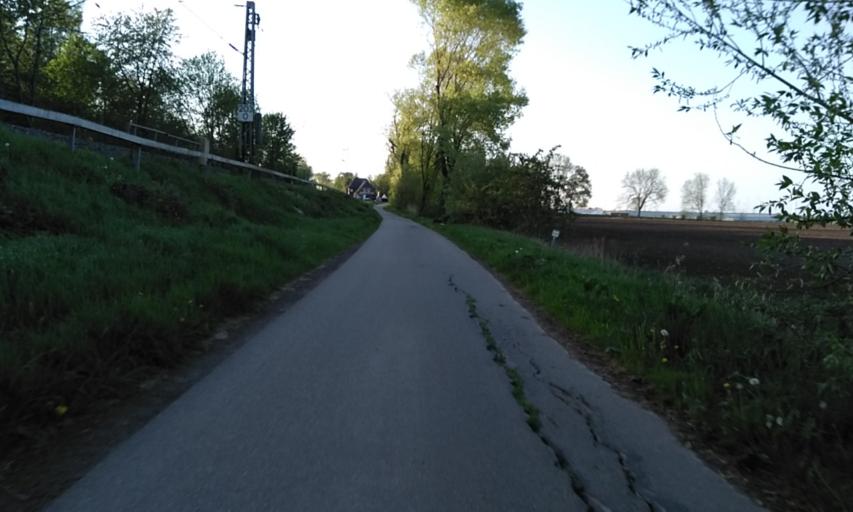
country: DE
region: Lower Saxony
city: Dollern
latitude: 53.5430
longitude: 9.5600
